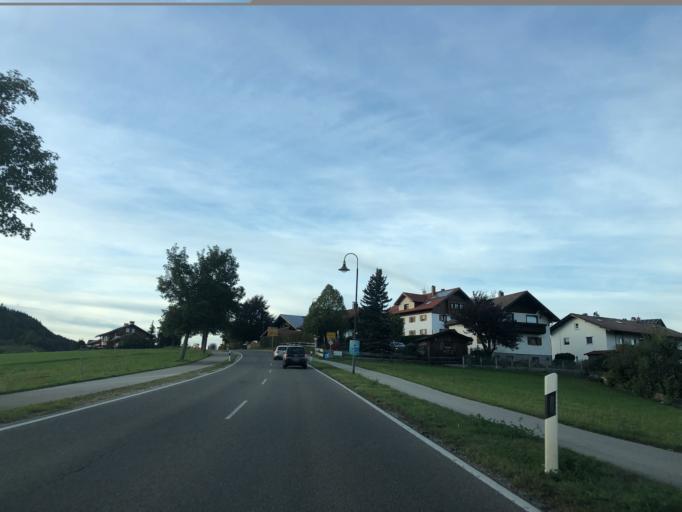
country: DE
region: Bavaria
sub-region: Swabia
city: Pfronten
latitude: 47.5919
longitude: 10.5570
